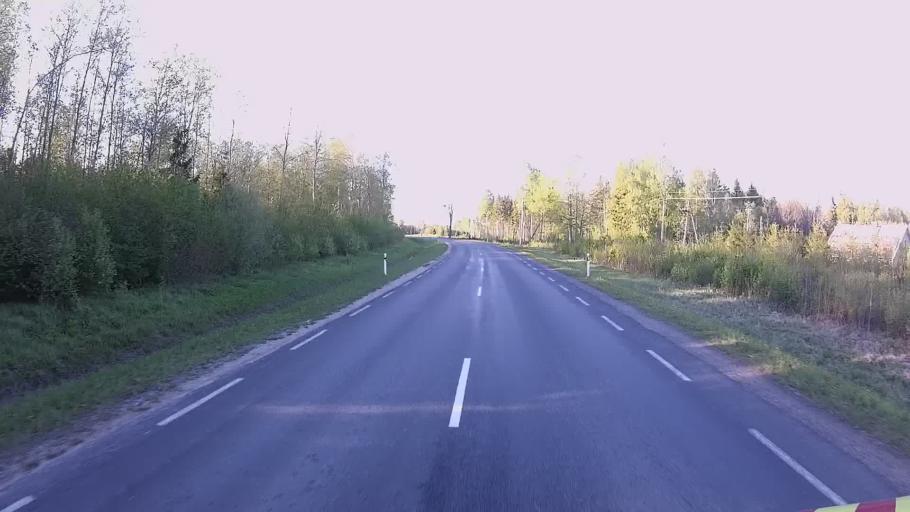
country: EE
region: Viljandimaa
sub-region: Viiratsi vald
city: Viiratsi
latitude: 58.4582
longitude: 25.7485
